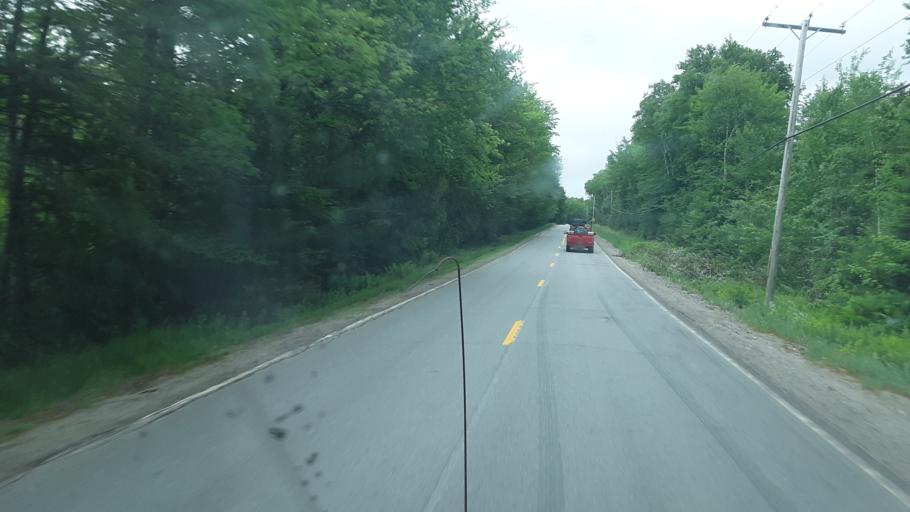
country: US
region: Maine
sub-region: Penobscot County
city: Millinocket
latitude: 45.6796
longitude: -68.7530
